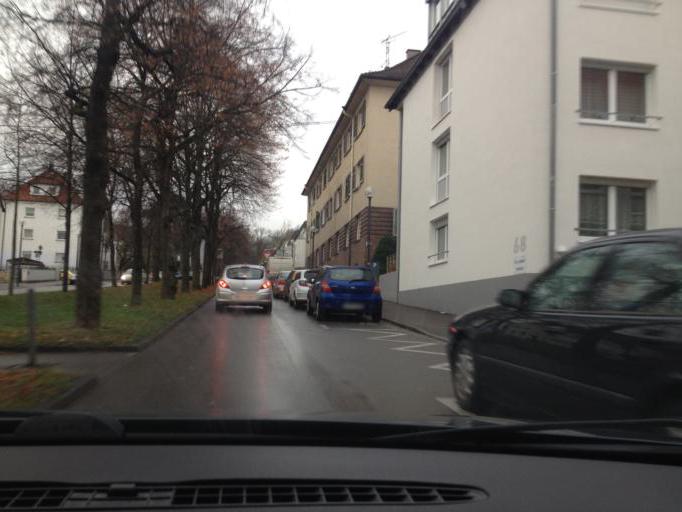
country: DE
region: Baden-Wuerttemberg
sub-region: Regierungsbezirk Stuttgart
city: Ludwigsburg
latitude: 48.8902
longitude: 9.2030
